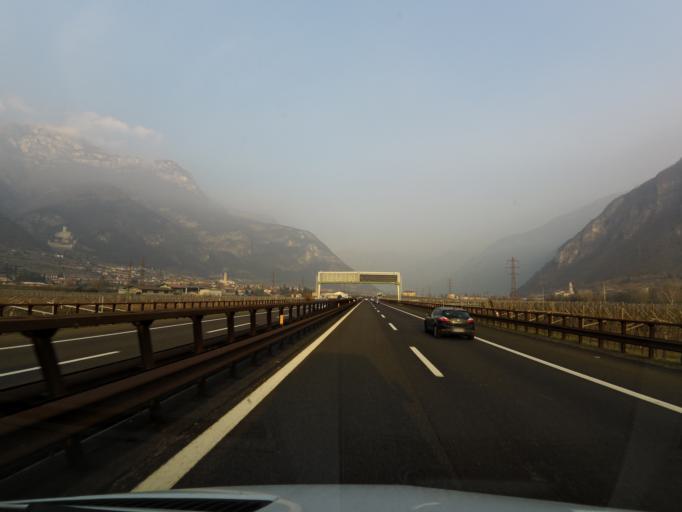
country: IT
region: Trentino-Alto Adige
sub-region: Provincia di Trento
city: Avio
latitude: 45.7337
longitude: 10.9489
